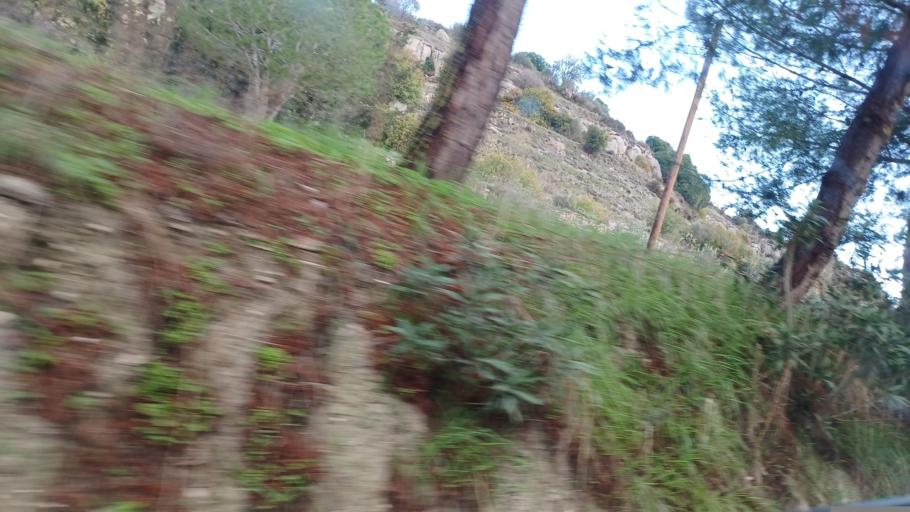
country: CY
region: Pafos
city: Mesogi
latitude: 34.8554
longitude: 32.5174
